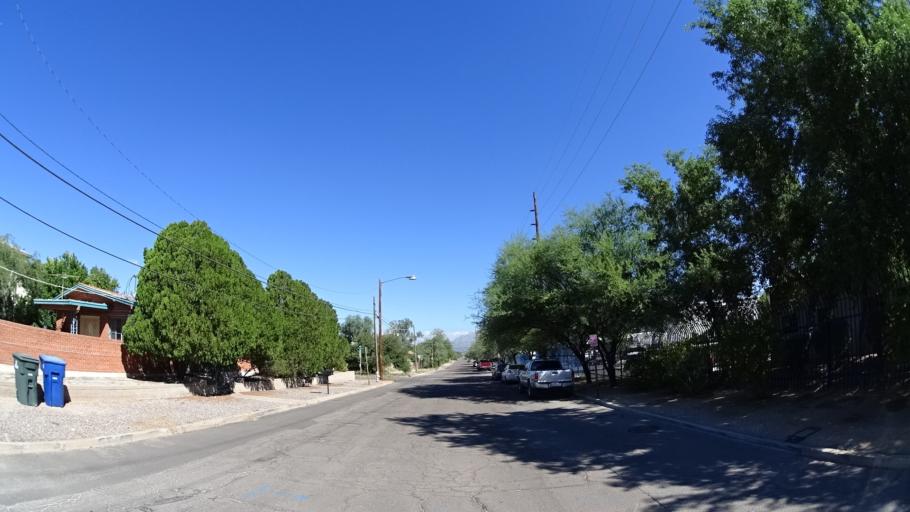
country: US
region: Arizona
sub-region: Pima County
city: Tucson
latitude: 32.2422
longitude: -110.9497
